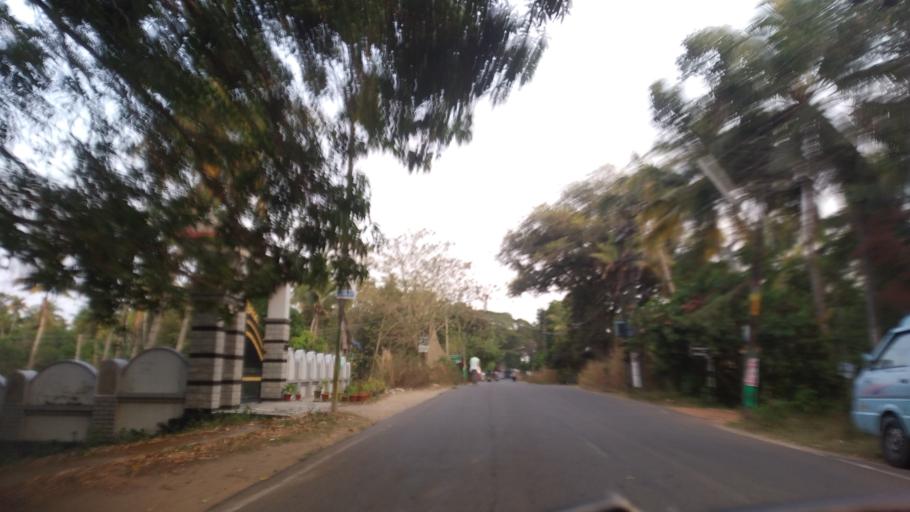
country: IN
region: Kerala
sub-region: Thrissur District
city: Kodungallur
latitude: 10.2200
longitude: 76.1589
